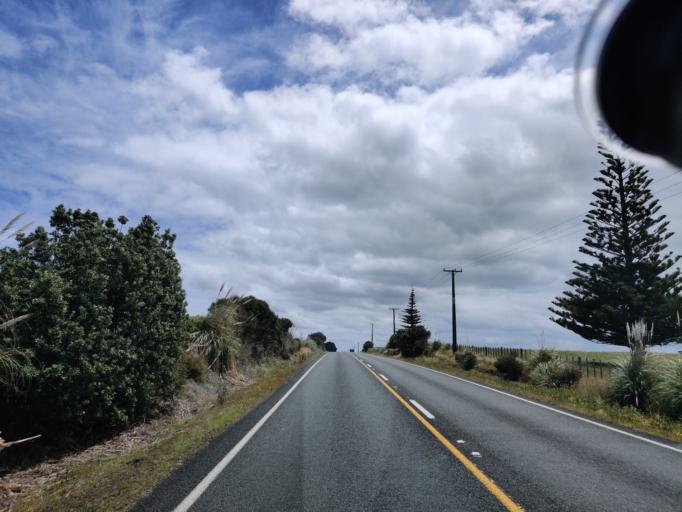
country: NZ
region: Northland
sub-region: Far North District
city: Kaitaia
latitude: -34.7004
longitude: 173.0278
